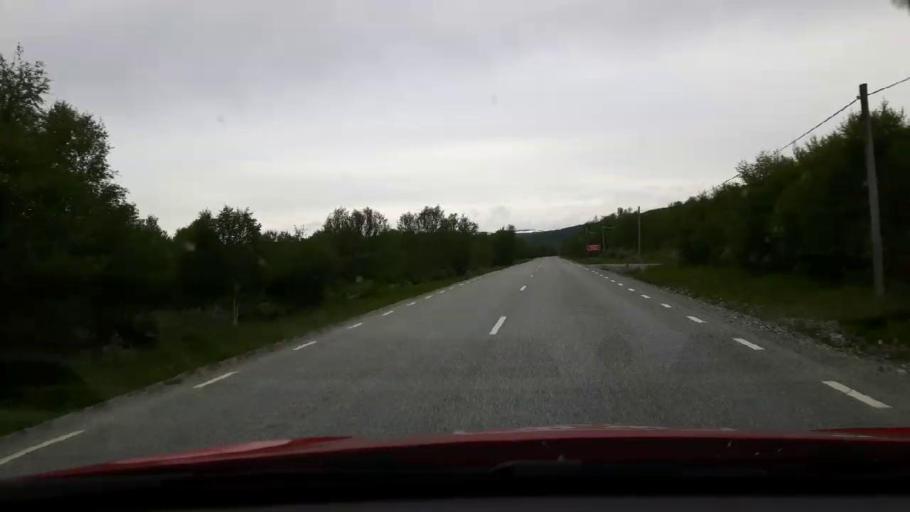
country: NO
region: Sor-Trondelag
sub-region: Tydal
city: Aas
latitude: 62.6905
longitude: 12.4099
